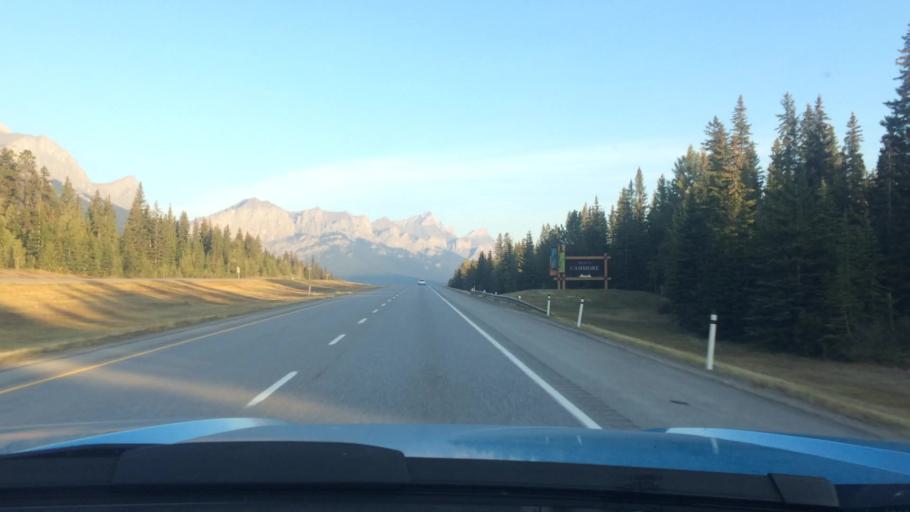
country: CA
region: Alberta
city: Canmore
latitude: 51.0436
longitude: -115.2863
